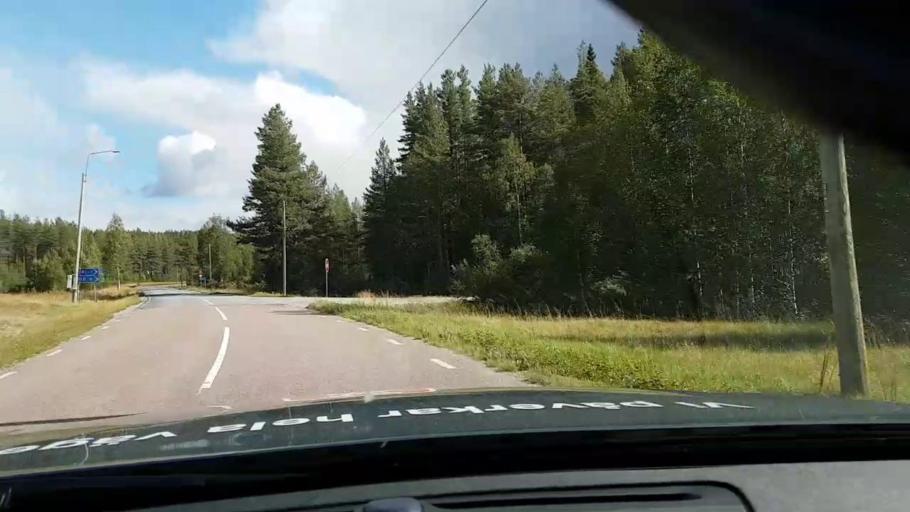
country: SE
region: Vaesterbotten
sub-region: Asele Kommun
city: Asele
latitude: 63.8605
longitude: 17.3737
